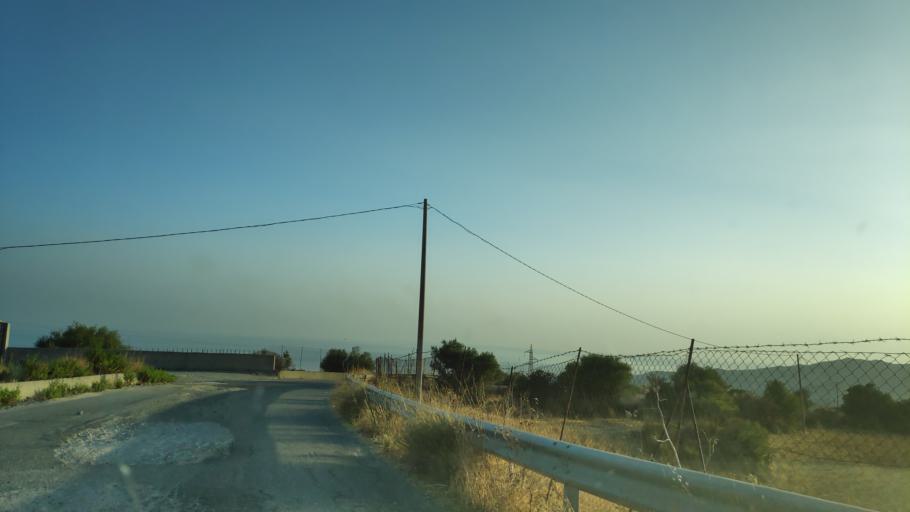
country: IT
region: Calabria
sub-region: Provincia di Reggio Calabria
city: Bova Marina
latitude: 37.9604
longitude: 15.9206
